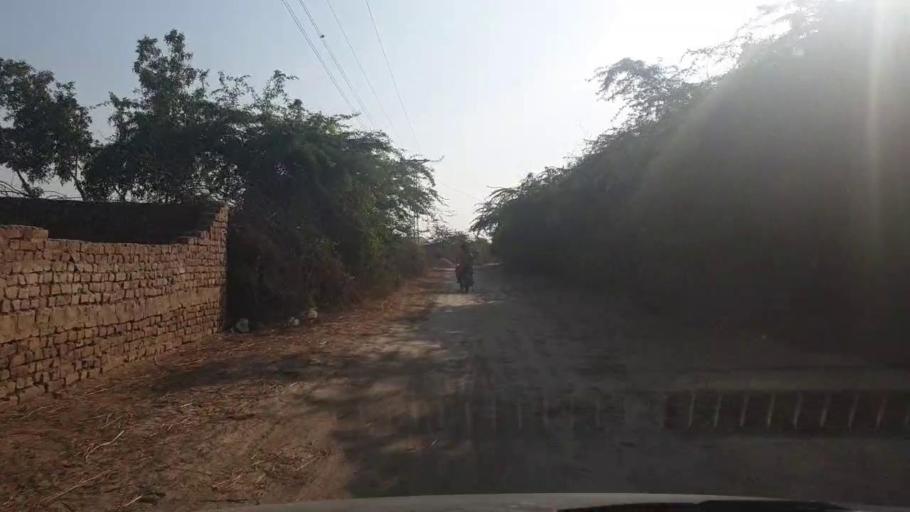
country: PK
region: Sindh
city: Badin
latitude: 24.6457
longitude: 68.8043
